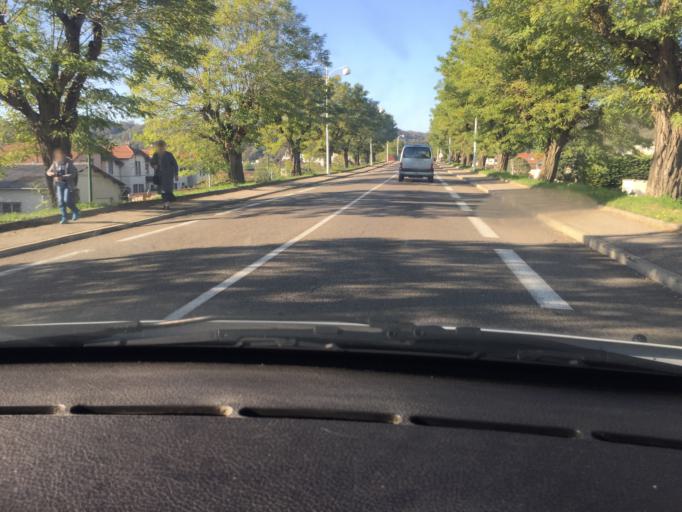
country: FR
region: Rhone-Alpes
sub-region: Departement de l'Ain
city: Saint-Maurice-de-Beynost
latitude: 45.8268
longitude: 4.9811
